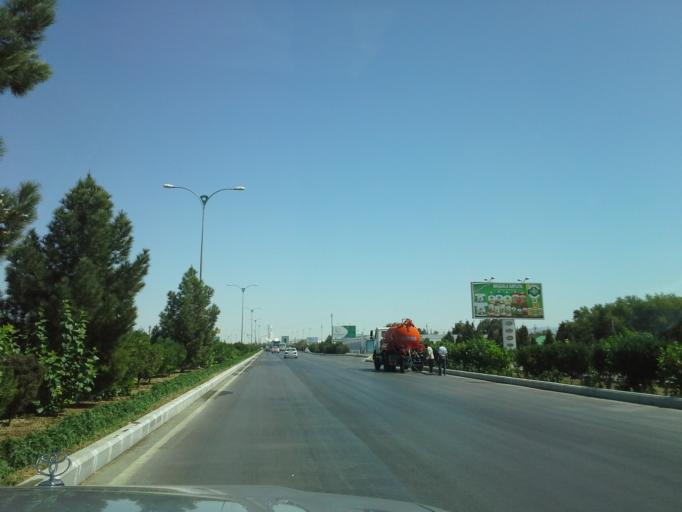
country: TM
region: Ahal
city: Annau
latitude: 37.9089
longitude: 58.5058
